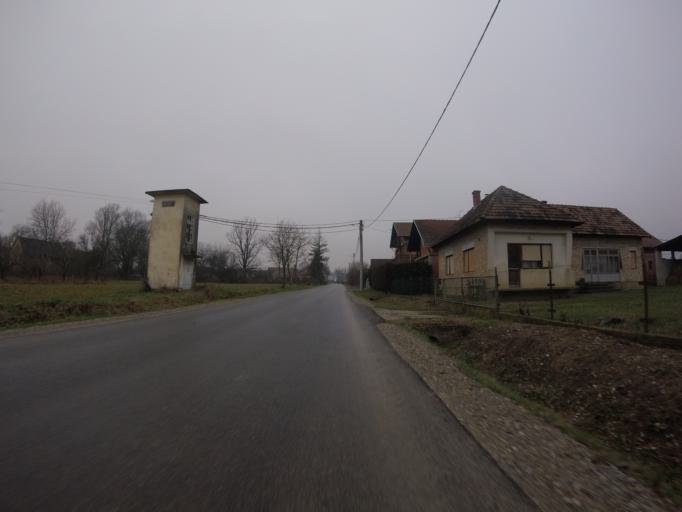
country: HR
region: Sisacko-Moslavacka
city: Lekenik
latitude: 45.6518
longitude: 16.2697
